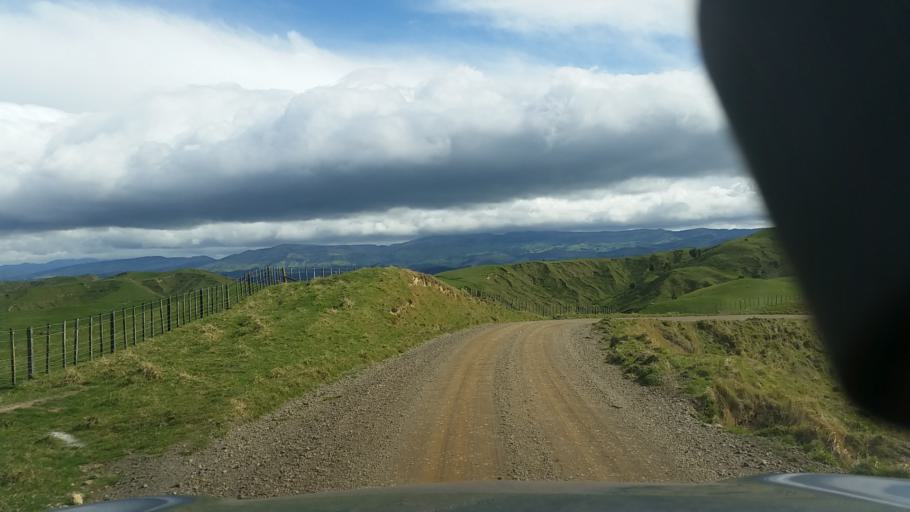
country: NZ
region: Hawke's Bay
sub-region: Napier City
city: Napier
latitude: -39.2086
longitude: 176.9568
